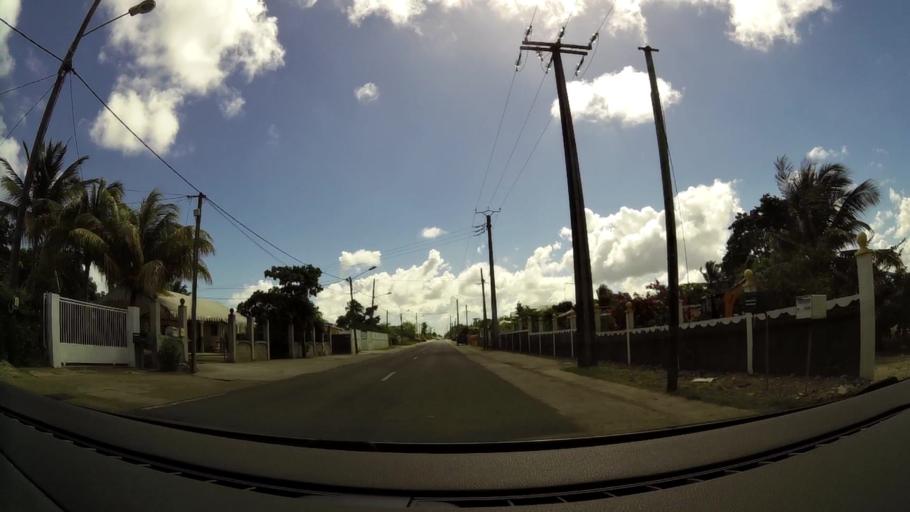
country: GP
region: Guadeloupe
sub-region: Guadeloupe
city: Petit-Canal
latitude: 16.4178
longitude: -61.4721
